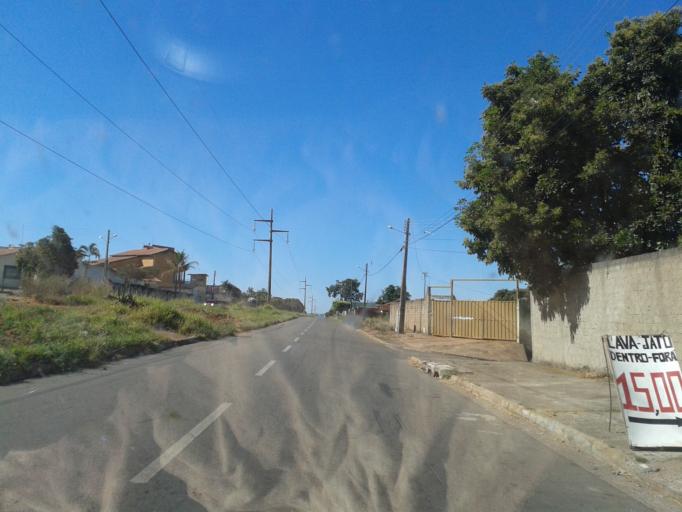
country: BR
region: Goias
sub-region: Aparecida De Goiania
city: Aparecida de Goiania
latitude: -16.7583
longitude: -49.3108
